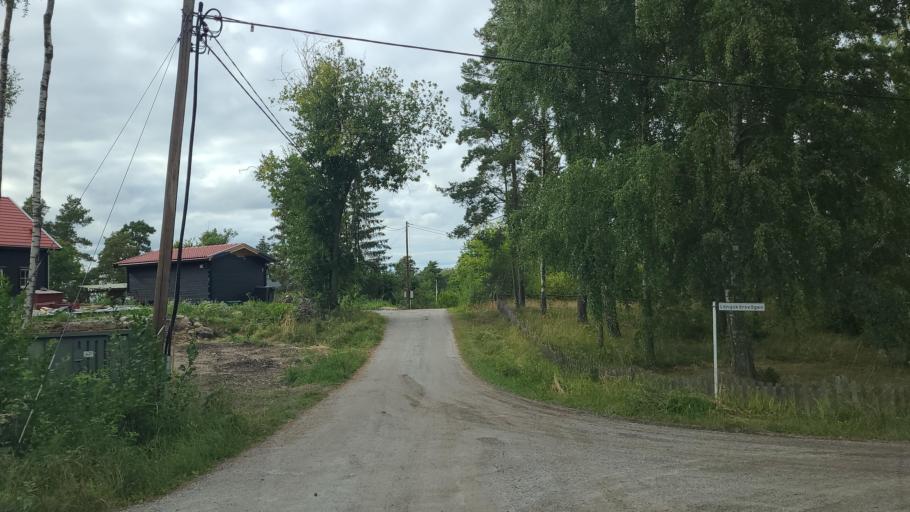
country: SE
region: Uppsala
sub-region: Habo Kommun
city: Balsta
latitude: 59.4761
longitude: 17.5487
